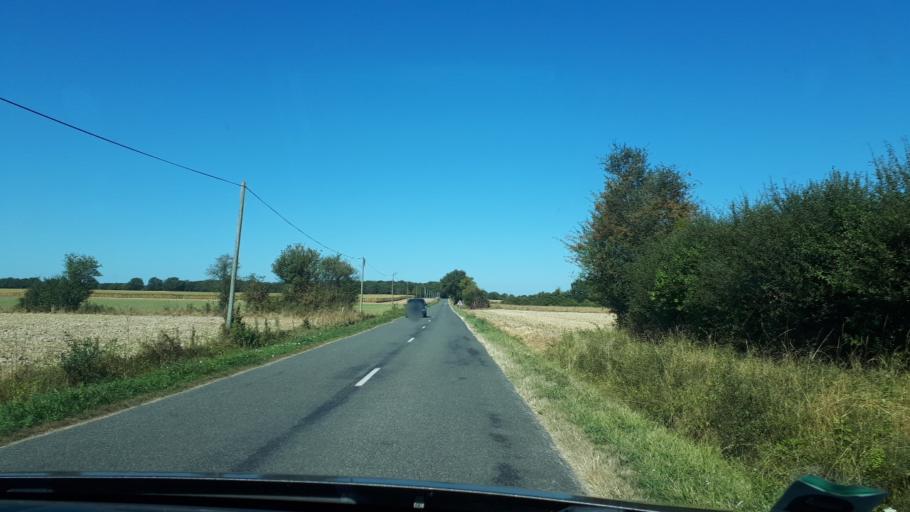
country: FR
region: Centre
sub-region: Departement du Loiret
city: Briare
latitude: 47.5918
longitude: 2.7186
